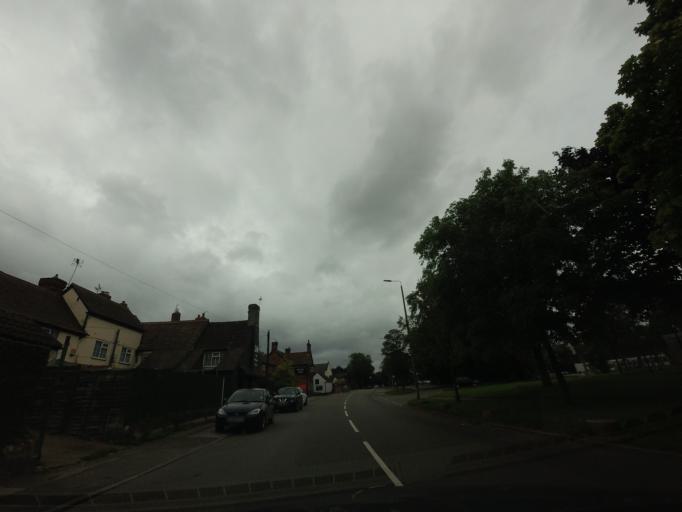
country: GB
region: England
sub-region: Nottinghamshire
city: Kimberley
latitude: 53.0055
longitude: -1.2523
